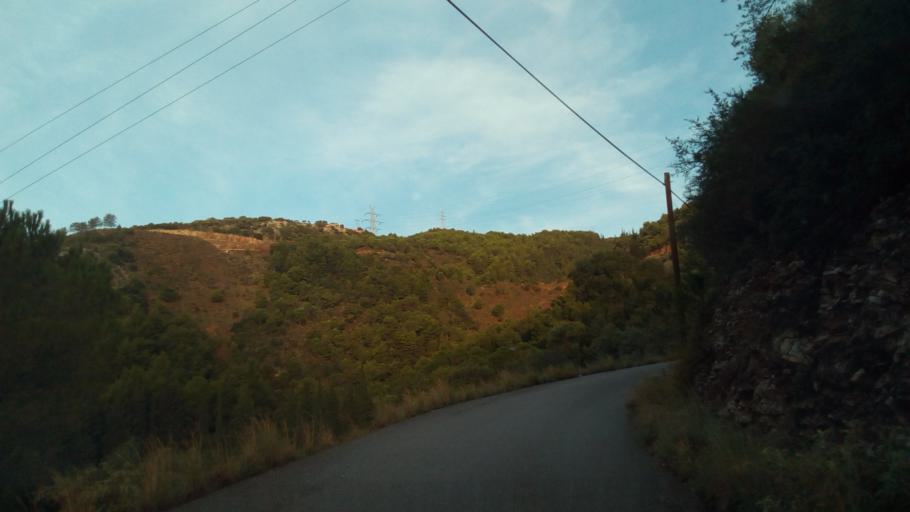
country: GR
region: West Greece
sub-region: Nomos Aitolias kai Akarnanias
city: Nafpaktos
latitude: 38.3988
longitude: 21.8316
